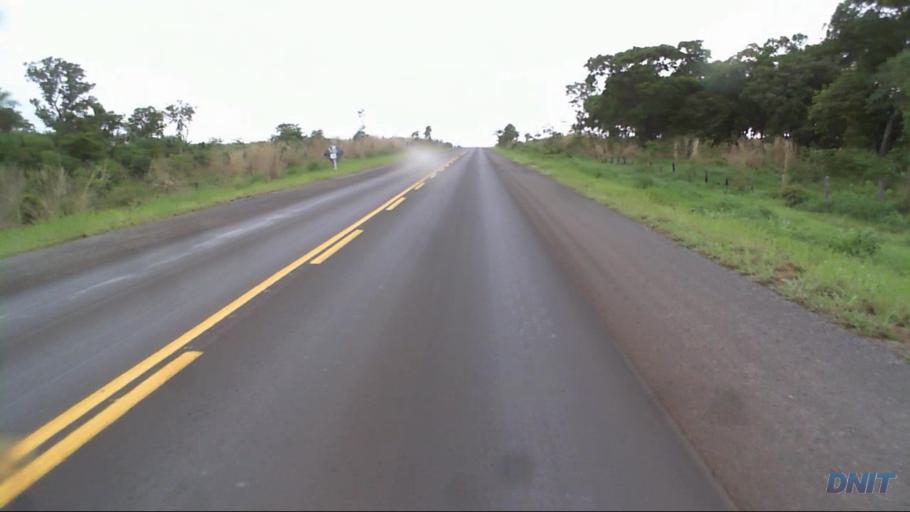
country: BR
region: Goias
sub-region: Padre Bernardo
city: Padre Bernardo
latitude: -15.2102
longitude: -48.4817
